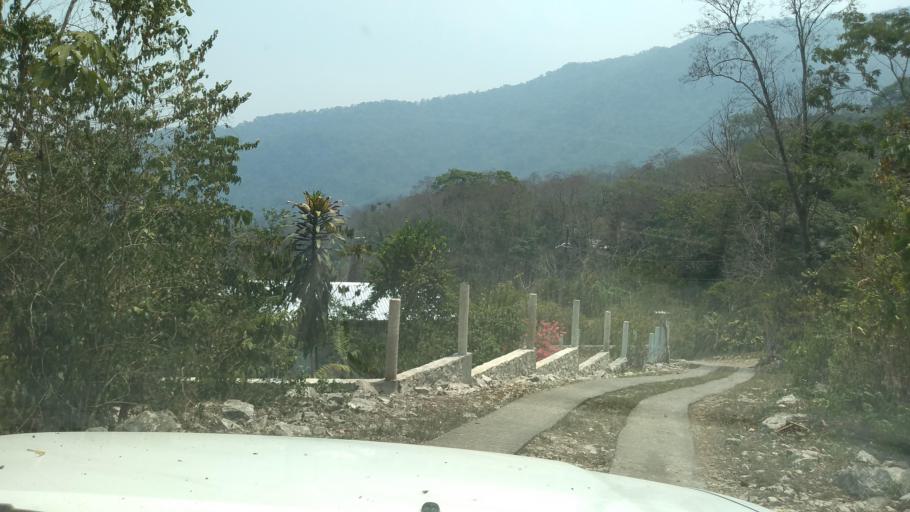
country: MX
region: Veracruz
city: Cosolapa
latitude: 18.5971
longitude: -96.7272
